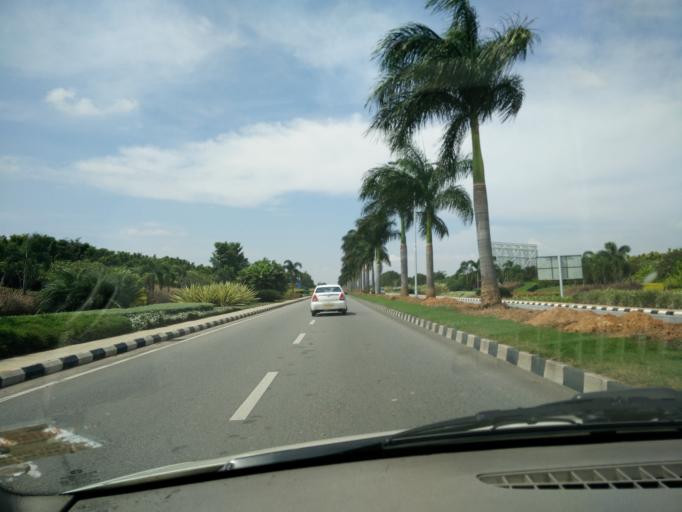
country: IN
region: Karnataka
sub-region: Bangalore Rural
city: Devanhalli
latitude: 13.1980
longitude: 77.6949
